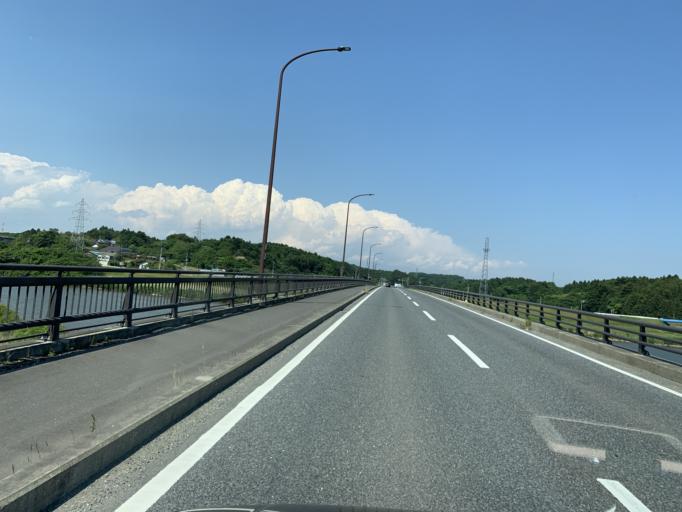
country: JP
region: Miyagi
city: Yamoto
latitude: 38.4132
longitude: 141.1435
